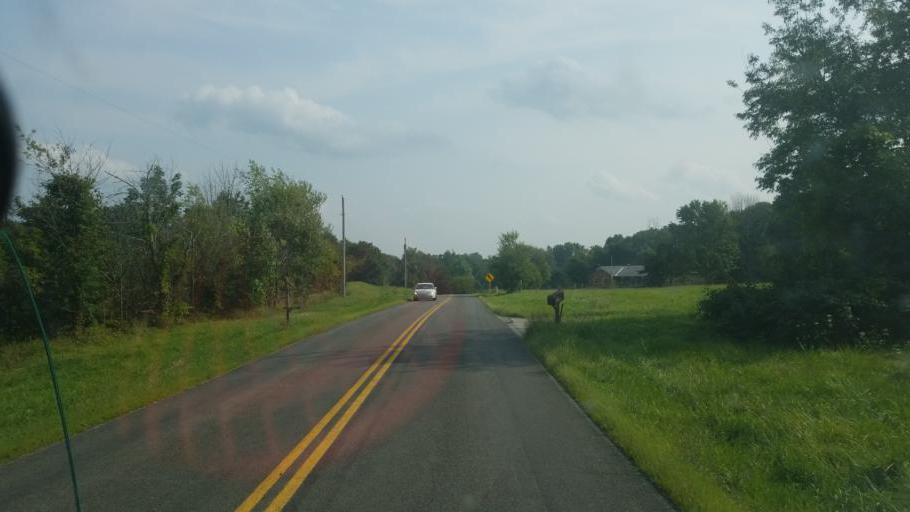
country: US
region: Ohio
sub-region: Medina County
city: Seville
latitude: 41.0651
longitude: -81.8844
